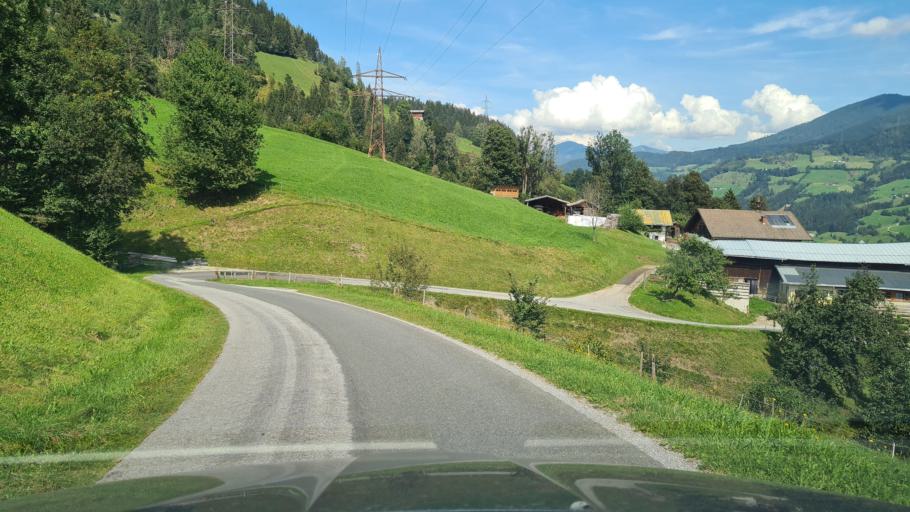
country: AT
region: Salzburg
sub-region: Politischer Bezirk Sankt Johann im Pongau
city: Sankt Johann im Pongau
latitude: 47.3588
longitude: 13.1888
